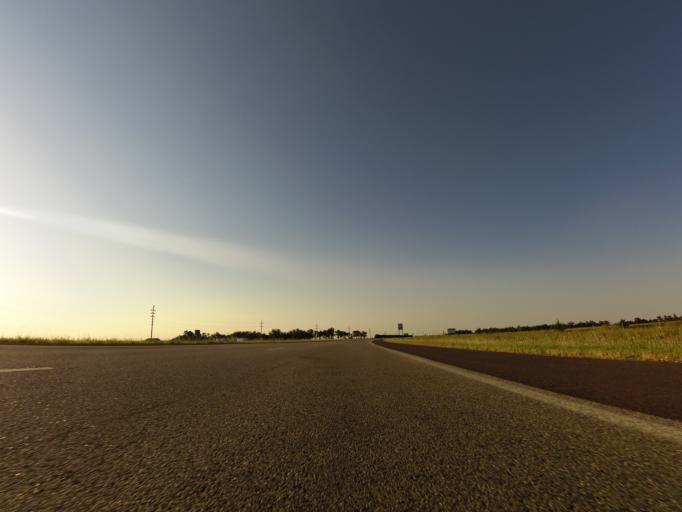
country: US
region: Kansas
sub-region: Reno County
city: South Hutchinson
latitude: 37.9760
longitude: -97.9392
